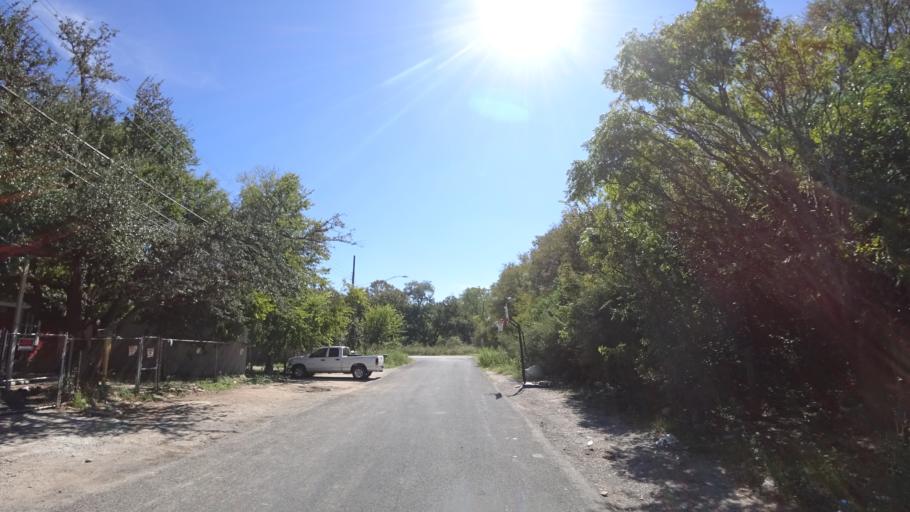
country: US
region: Texas
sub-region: Travis County
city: Austin
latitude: 30.2748
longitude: -97.6808
